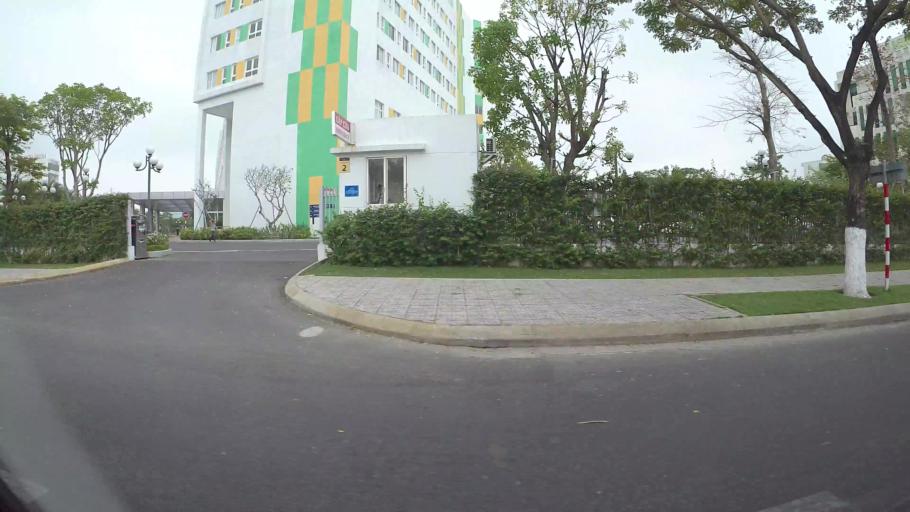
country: VN
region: Da Nang
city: Cam Le
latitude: 16.0388
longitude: 108.2106
